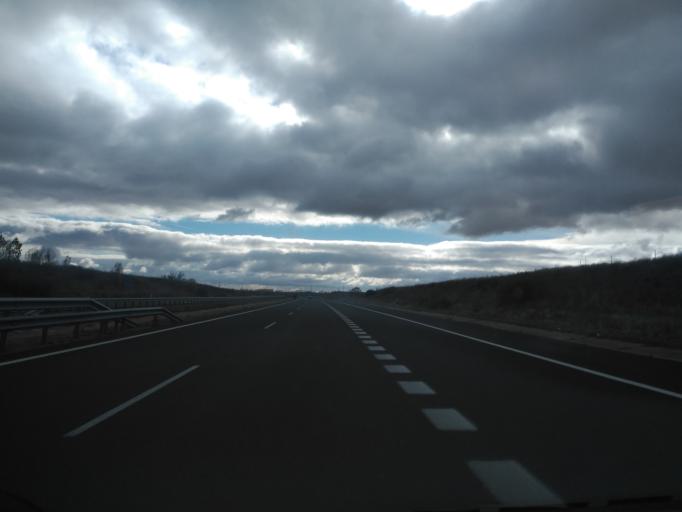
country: ES
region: Castille and Leon
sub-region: Provincia de Palencia
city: Abia de las Torres
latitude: 42.4333
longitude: -4.3934
